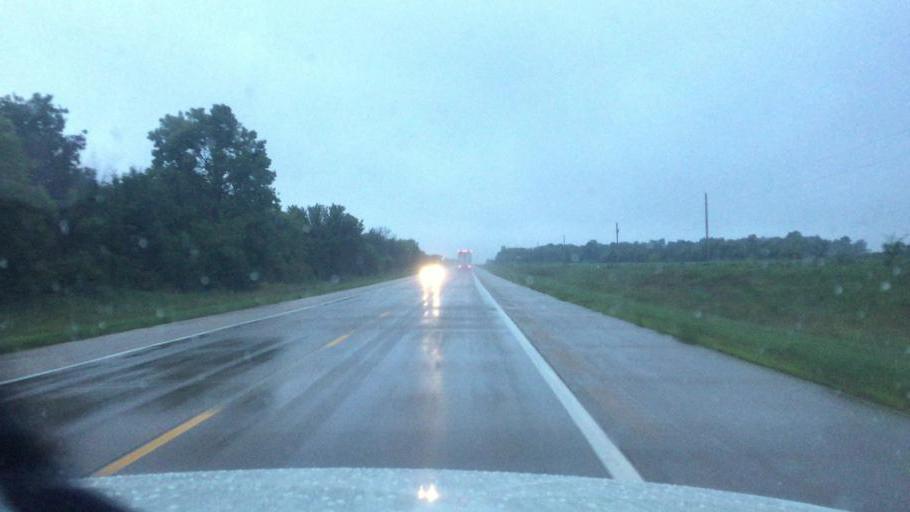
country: US
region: Kansas
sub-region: Neosho County
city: Chanute
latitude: 37.5525
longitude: -95.4709
